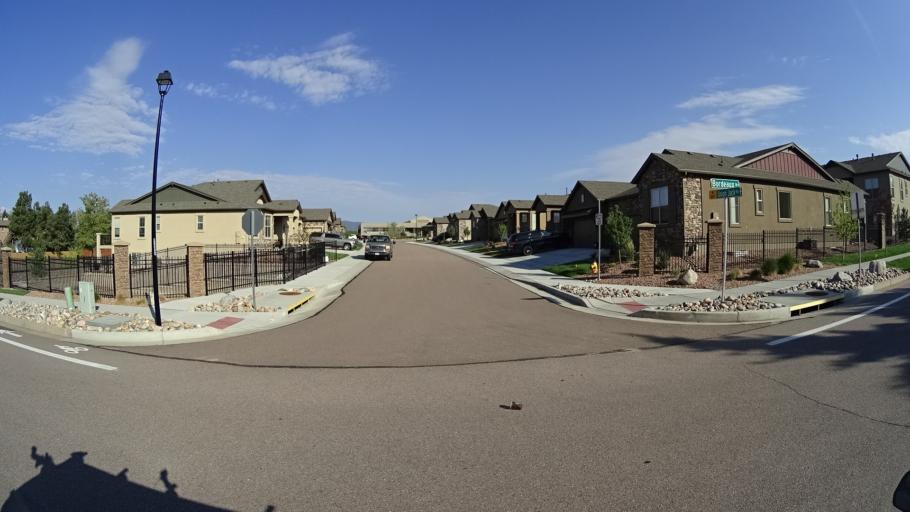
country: US
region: Colorado
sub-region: El Paso County
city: Black Forest
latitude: 38.9453
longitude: -104.7642
